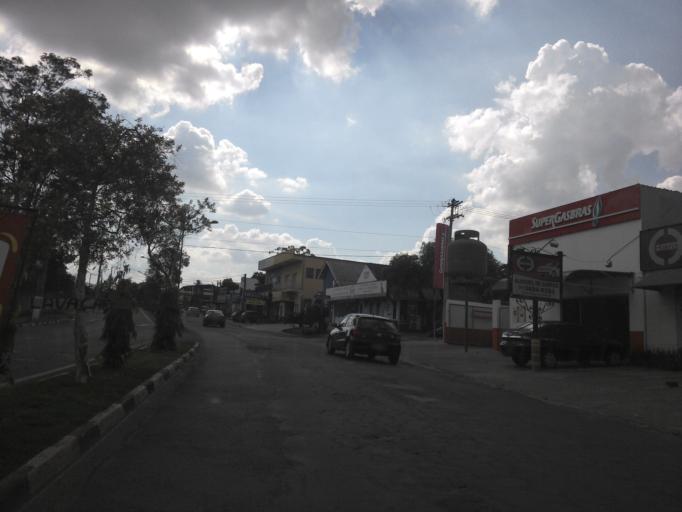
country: BR
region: Sao Paulo
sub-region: Vinhedo
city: Vinhedo
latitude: -23.0287
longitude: -46.9886
